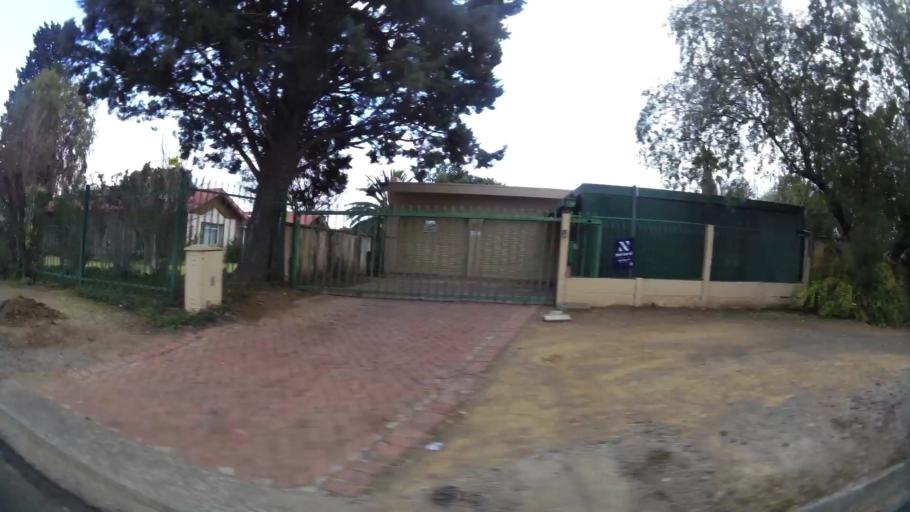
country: ZA
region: Orange Free State
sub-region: Mangaung Metropolitan Municipality
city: Bloemfontein
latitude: -29.1217
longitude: 26.1696
